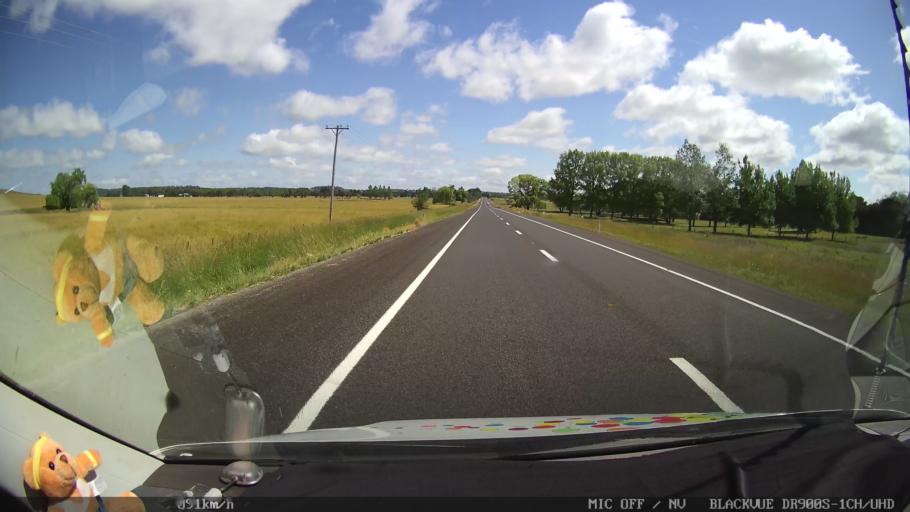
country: AU
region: New South Wales
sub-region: Glen Innes Severn
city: Glen Innes
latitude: -29.8324
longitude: 151.7376
